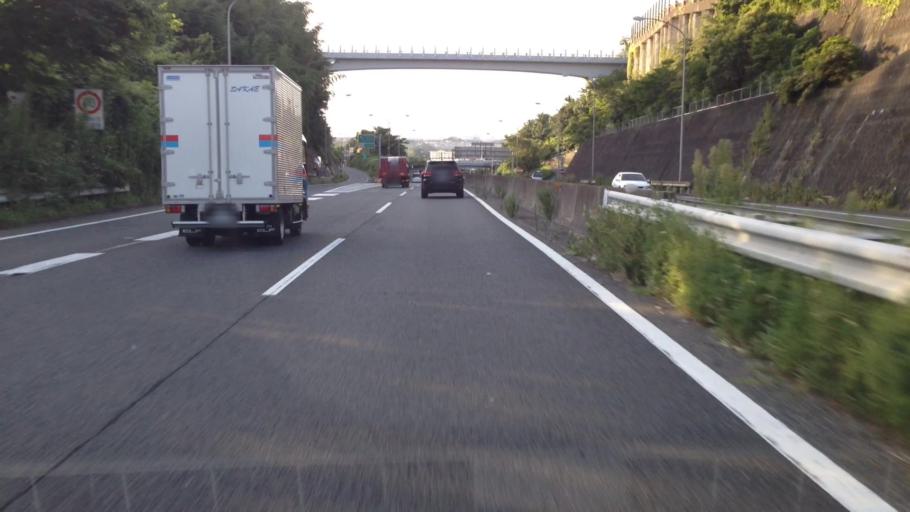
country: JP
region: Kanagawa
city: Kamakura
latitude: 35.3661
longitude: 139.5970
